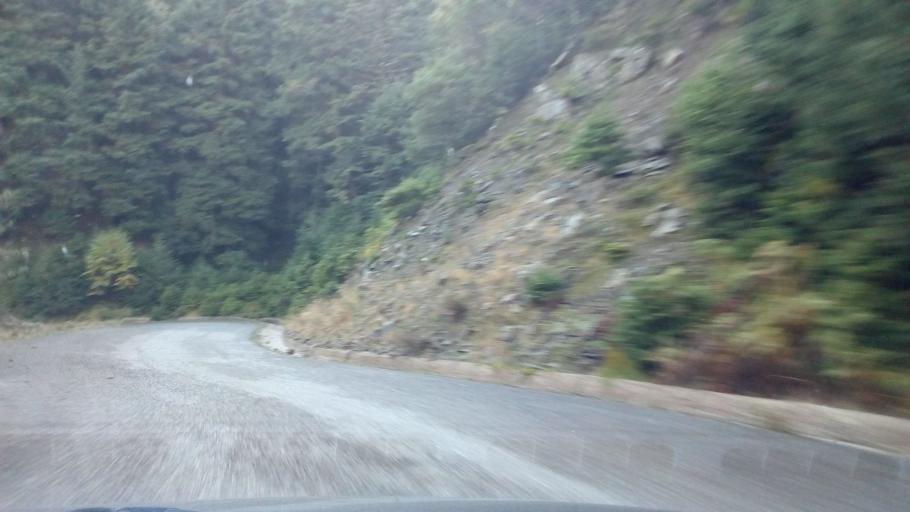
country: GR
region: West Greece
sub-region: Nomos Aitolias kai Akarnanias
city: Nafpaktos
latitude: 38.5350
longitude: 21.8457
